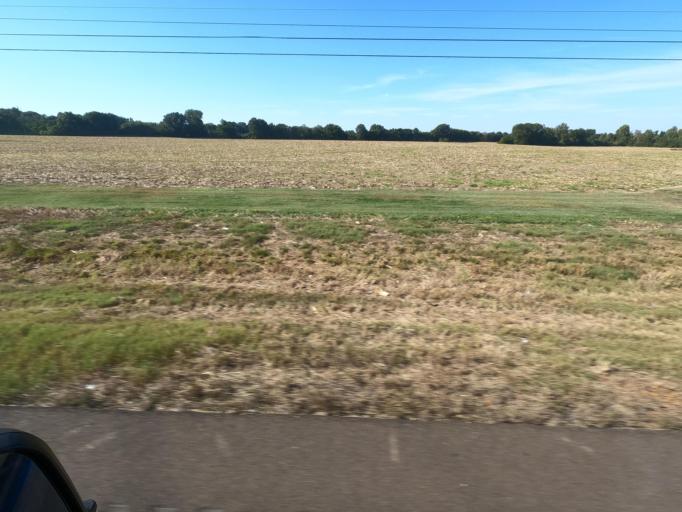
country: US
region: Tennessee
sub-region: Obion County
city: Englewood
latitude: 36.3880
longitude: -89.1044
